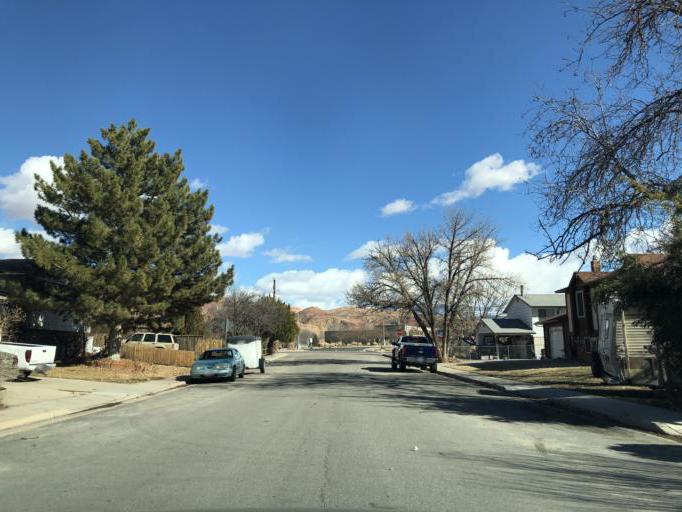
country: US
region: Utah
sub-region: Grand County
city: Moab
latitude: 38.5755
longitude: -109.5623
